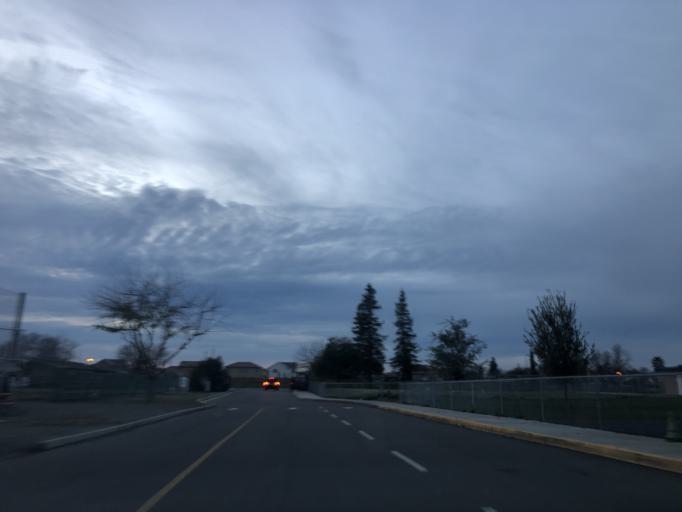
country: US
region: California
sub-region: Yolo County
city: Woodland
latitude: 38.6584
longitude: -121.7550
